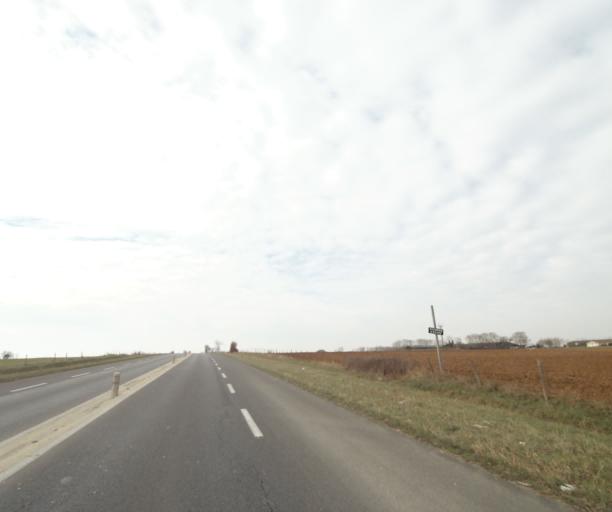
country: FR
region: Poitou-Charentes
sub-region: Departement des Deux-Sevres
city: Aiffres
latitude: 46.3097
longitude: -0.4280
